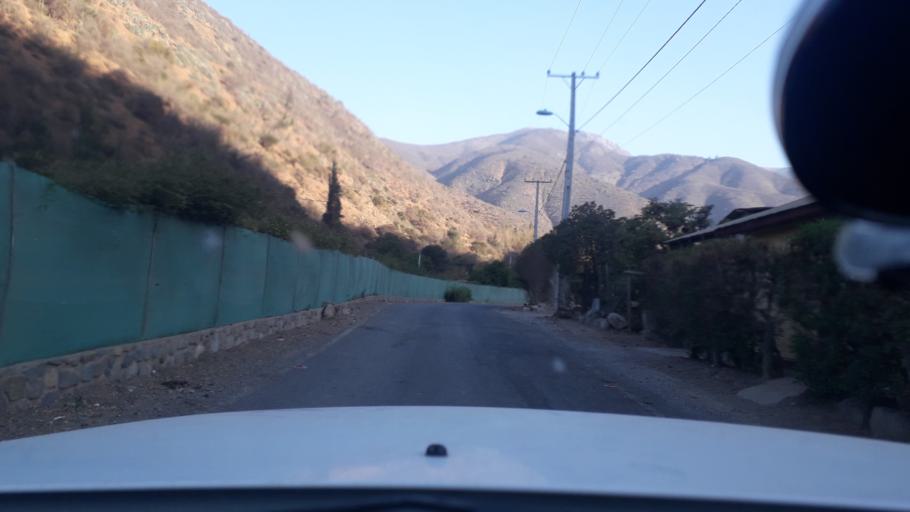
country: CL
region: Valparaiso
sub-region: Provincia de Marga Marga
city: Limache
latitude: -33.0631
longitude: -71.1174
